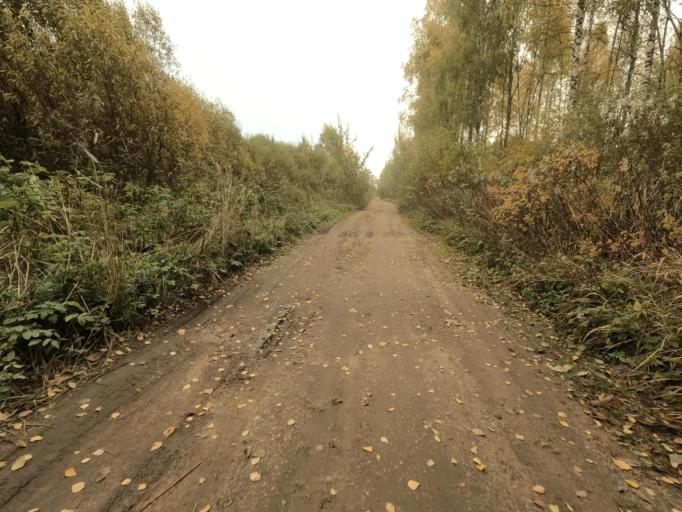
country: RU
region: Novgorod
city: Pankovka
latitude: 58.8714
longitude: 30.8938
